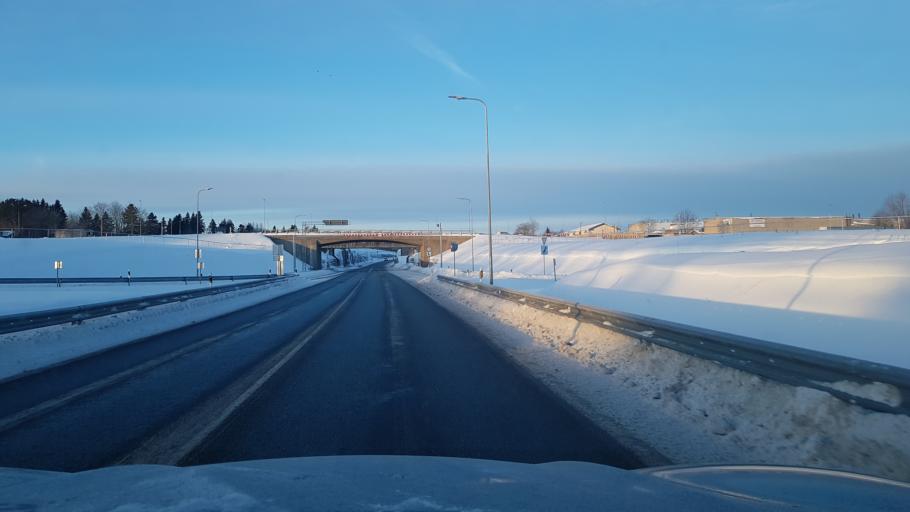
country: EE
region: Ida-Virumaa
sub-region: Sillamaee linn
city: Sillamae
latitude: 59.3912
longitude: 27.7527
